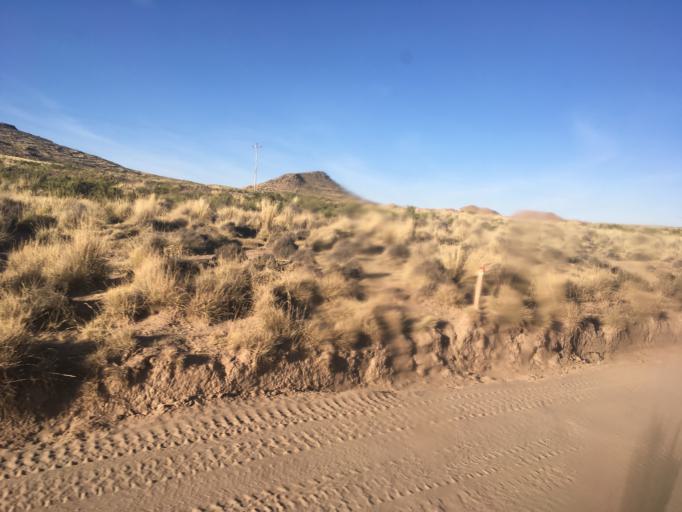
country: PE
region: Puno
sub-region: Provincia de Chucuito
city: Kelluyo
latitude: -16.9709
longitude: -69.0106
